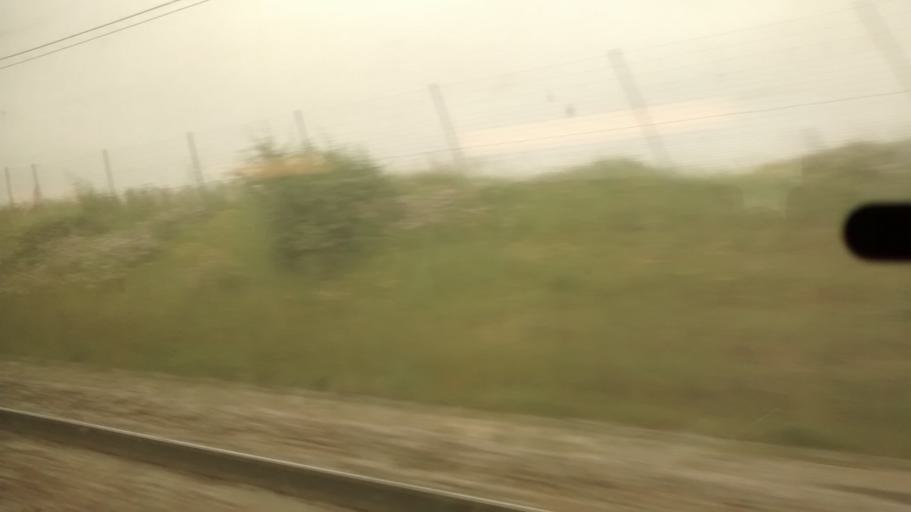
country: FR
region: Bourgogne
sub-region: Departement de l'Yonne
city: Sergines
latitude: 48.3101
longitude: 3.2443
